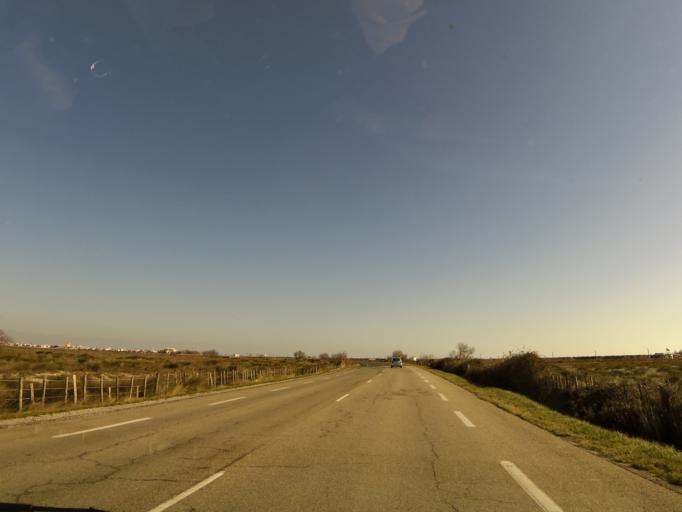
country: FR
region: Provence-Alpes-Cote d'Azur
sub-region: Departement des Bouches-du-Rhone
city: Saintes-Maries-de-la-Mer
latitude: 43.4518
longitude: 4.4029
